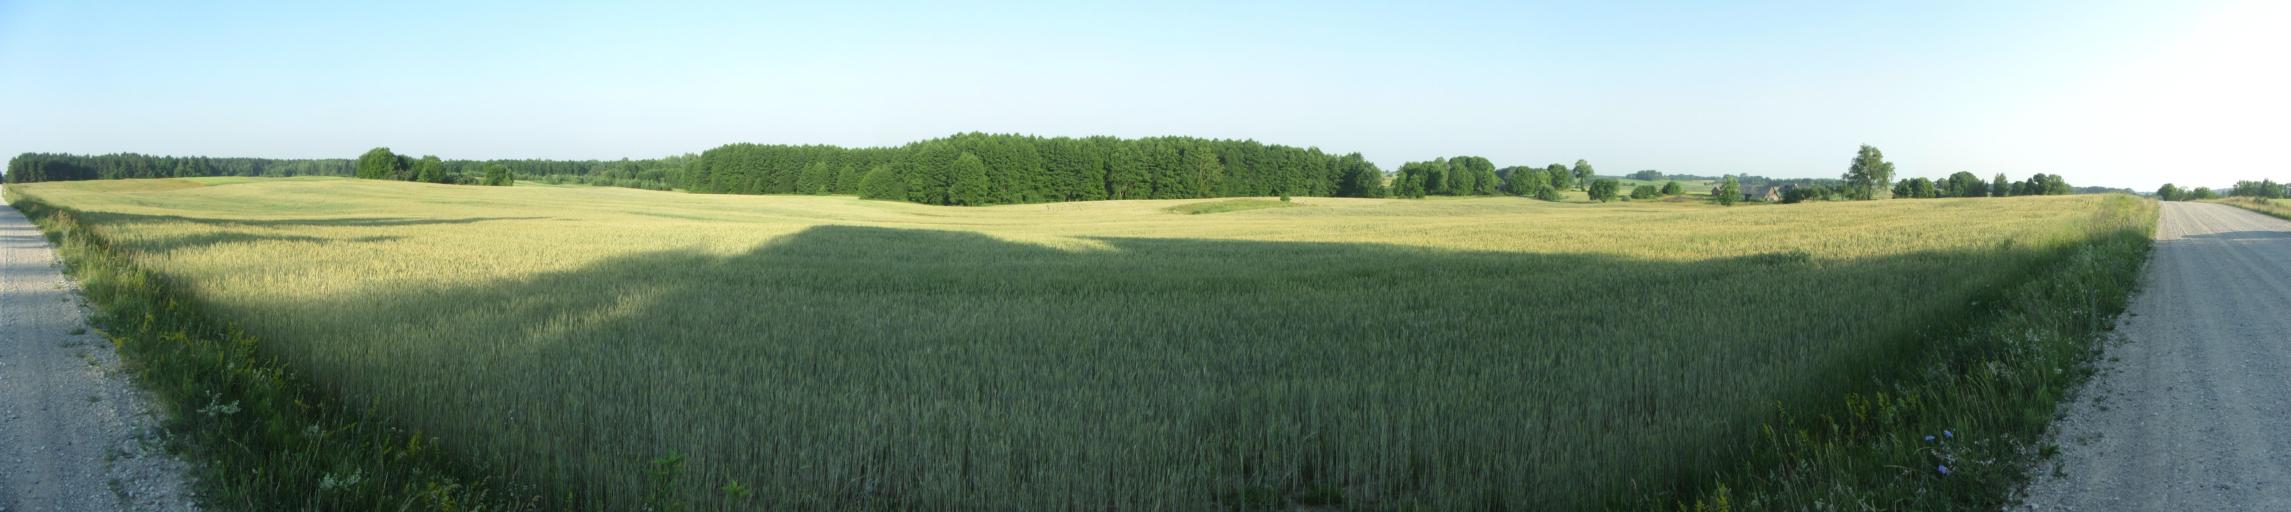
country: LT
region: Alytaus apskritis
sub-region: Alytus
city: Alytus
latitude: 54.2440
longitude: 23.9162
